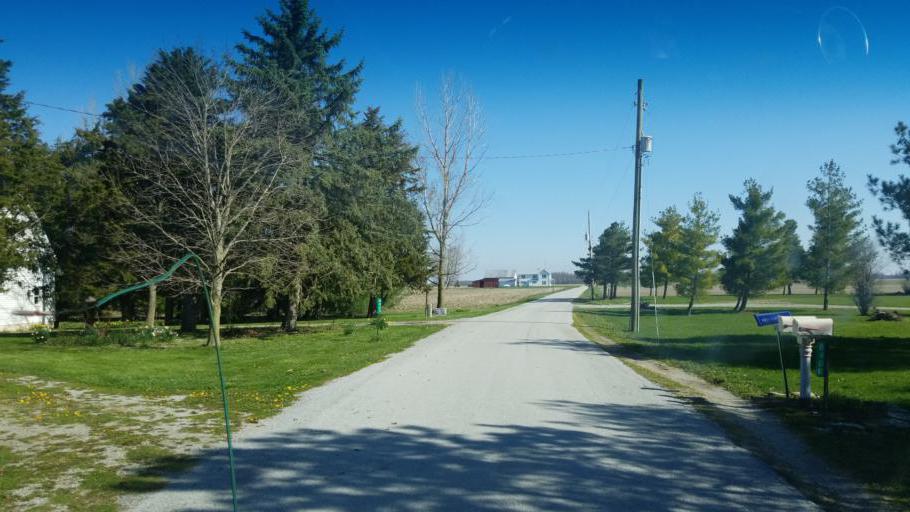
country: US
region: Ohio
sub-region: Hardin County
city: Kenton
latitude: 40.6961
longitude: -83.5603
